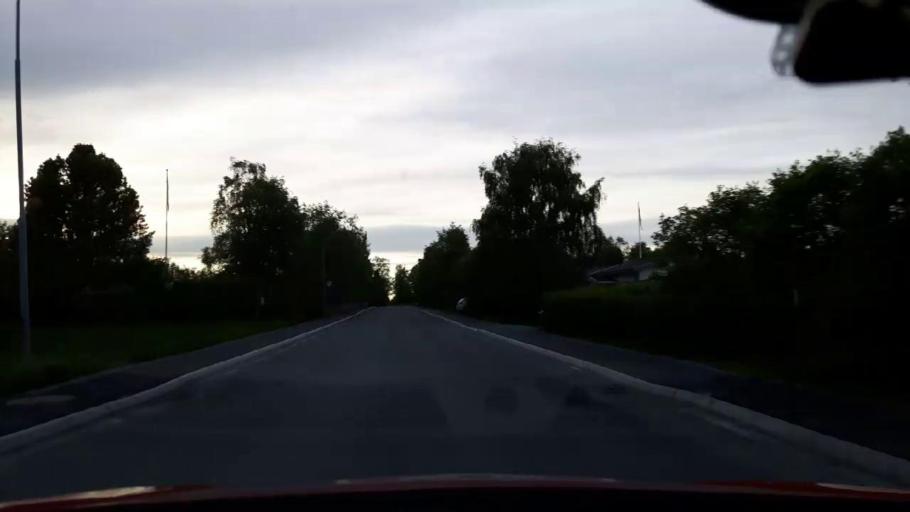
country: SE
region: Jaemtland
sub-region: OEstersunds Kommun
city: Ostersund
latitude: 62.9910
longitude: 14.5800
